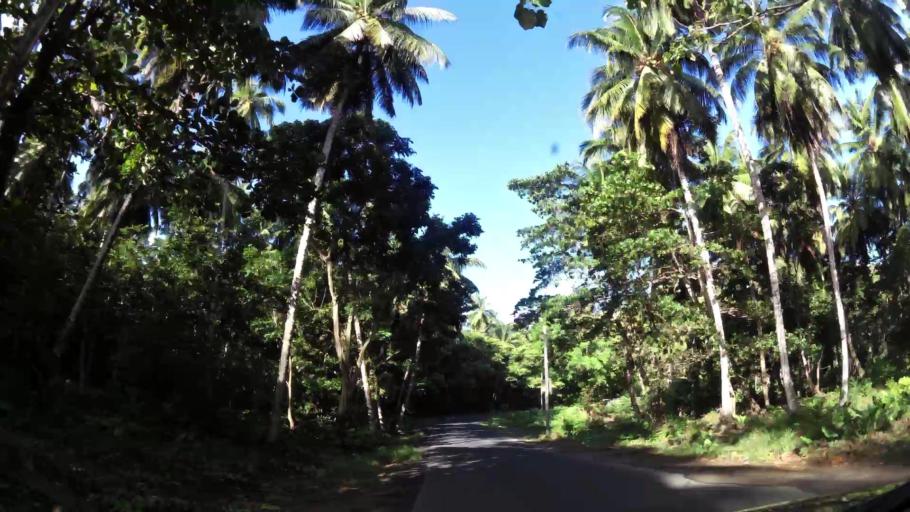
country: DM
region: Saint Andrew
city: Calibishie
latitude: 15.5929
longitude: -61.3629
